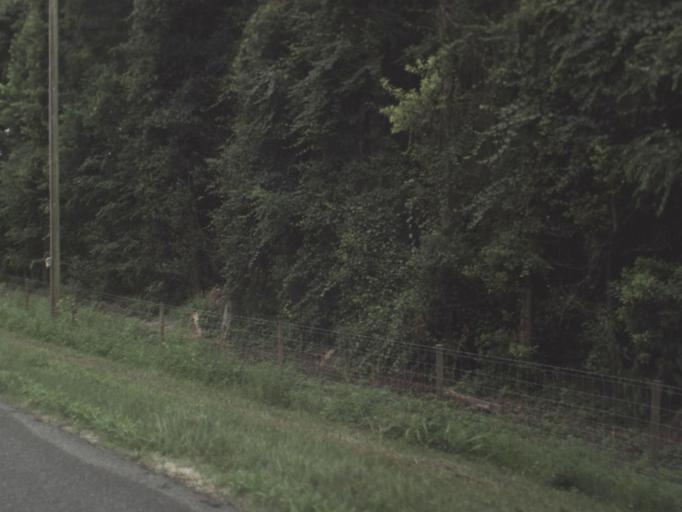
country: US
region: Florida
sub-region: Alachua County
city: Archer
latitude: 29.5600
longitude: -82.5348
